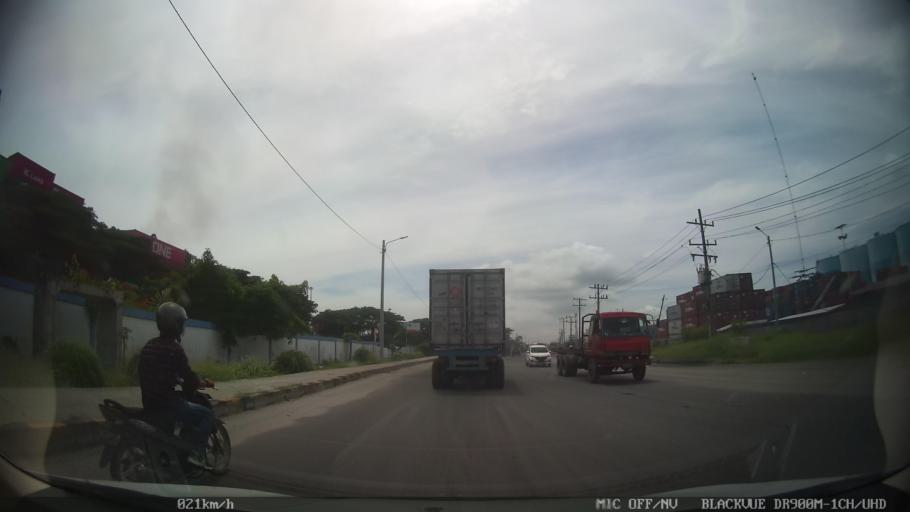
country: ID
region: North Sumatra
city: Belawan
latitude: 3.7809
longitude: 98.6964
